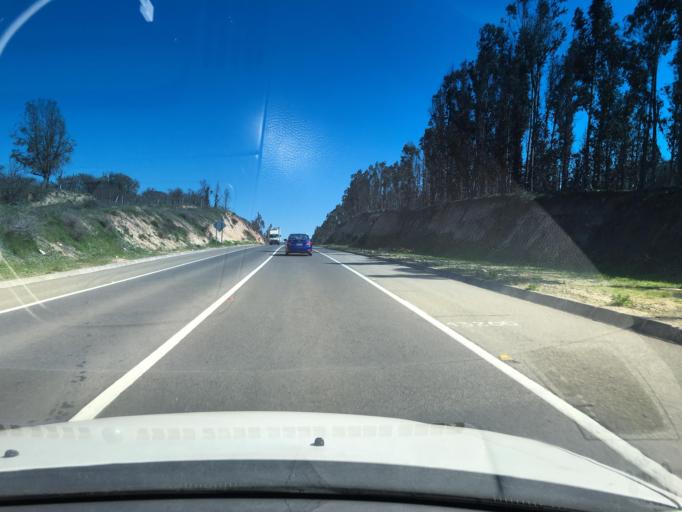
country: CL
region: Valparaiso
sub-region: San Antonio Province
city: El Tabo
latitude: -33.3920
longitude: -71.4824
